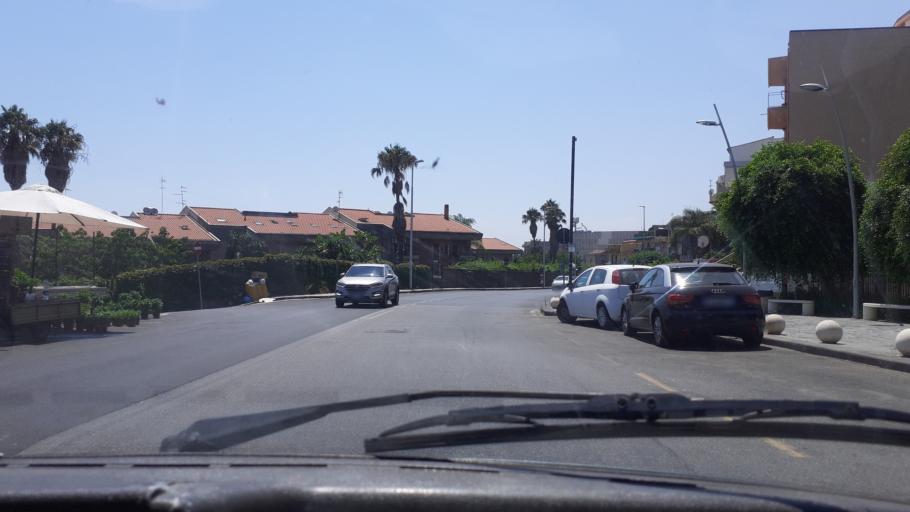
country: IT
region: Sicily
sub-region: Catania
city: Cerza
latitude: 37.5377
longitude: 15.1024
